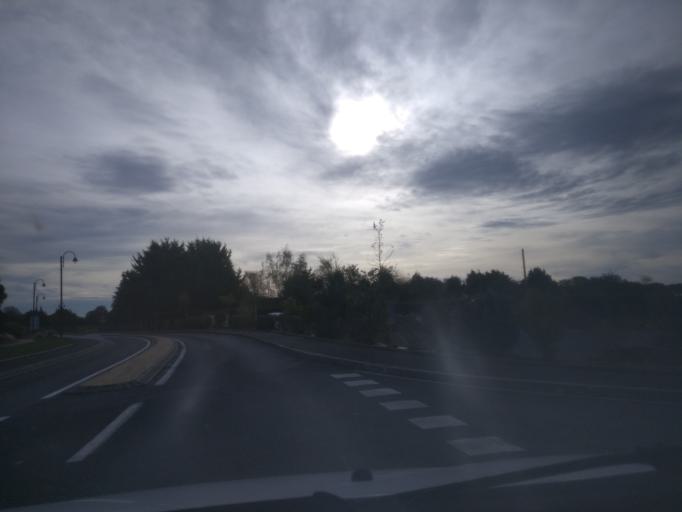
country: FR
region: Lower Normandy
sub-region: Departement de la Manche
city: Jullouville
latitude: 48.7466
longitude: -1.5538
